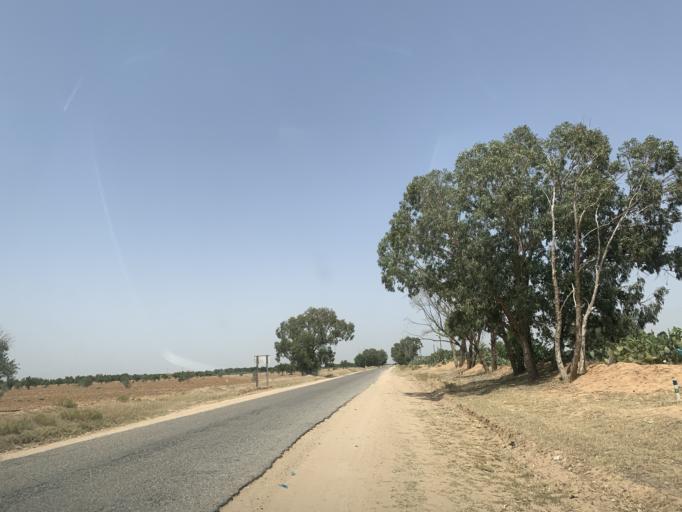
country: TN
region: Al Mahdiyah
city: Shurban
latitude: 35.1739
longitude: 10.2309
